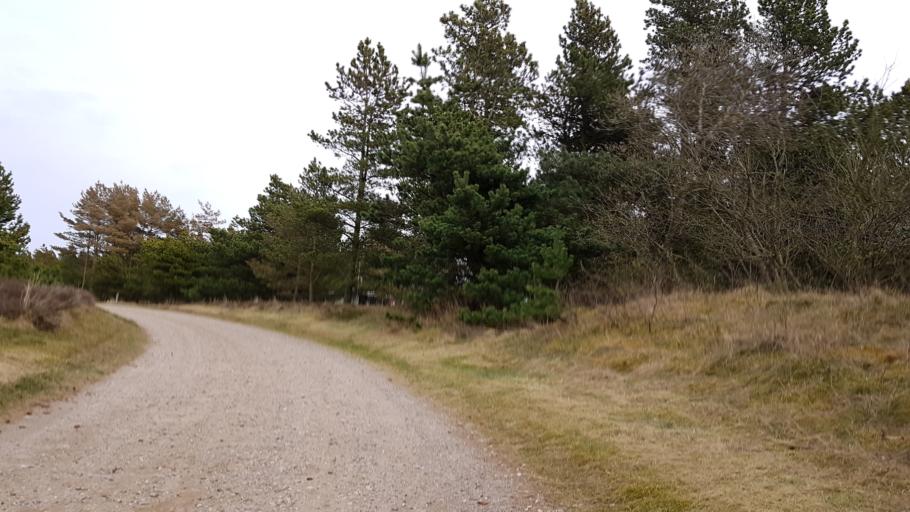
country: DE
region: Schleswig-Holstein
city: List
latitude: 55.1556
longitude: 8.5244
